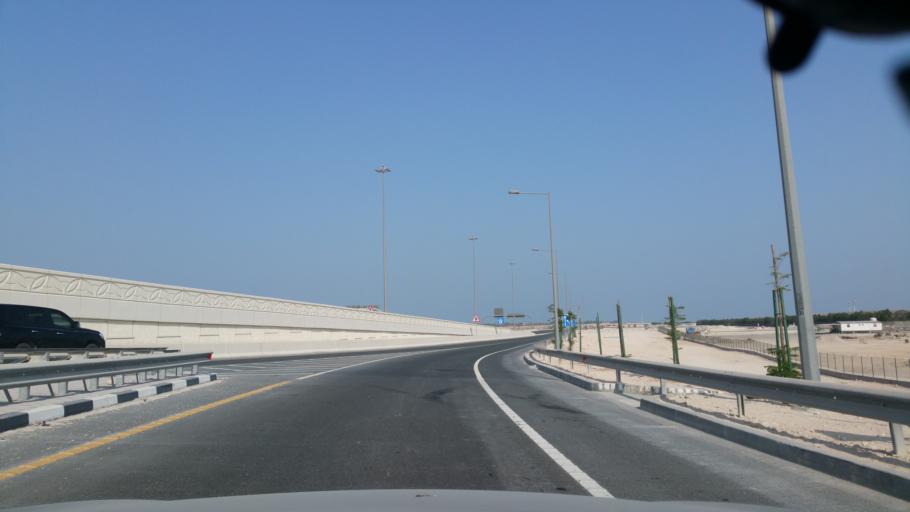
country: QA
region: Baladiyat Umm Salal
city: Umm Salal `Ali
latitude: 25.4565
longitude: 51.4812
